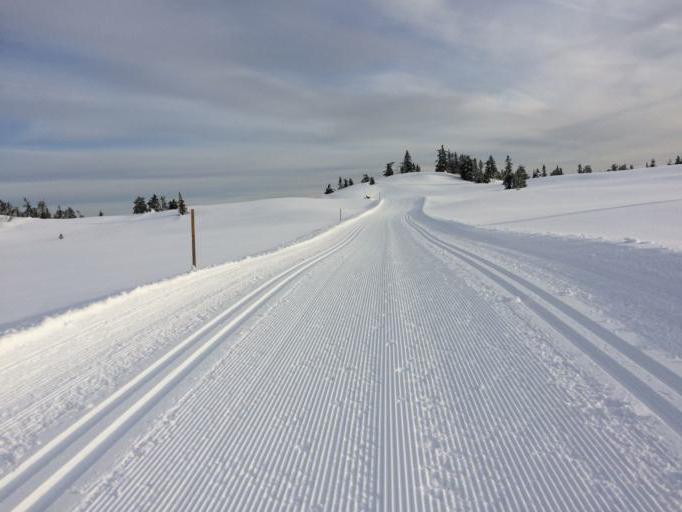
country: NO
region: Oppland
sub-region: Gausdal
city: Segalstad bru
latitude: 61.3256
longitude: 10.0390
